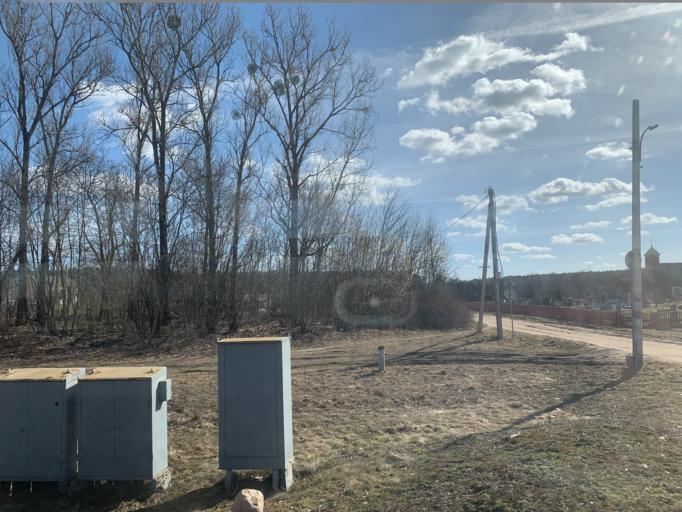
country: BY
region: Minsk
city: Stowbtsy
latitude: 53.5136
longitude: 26.8677
